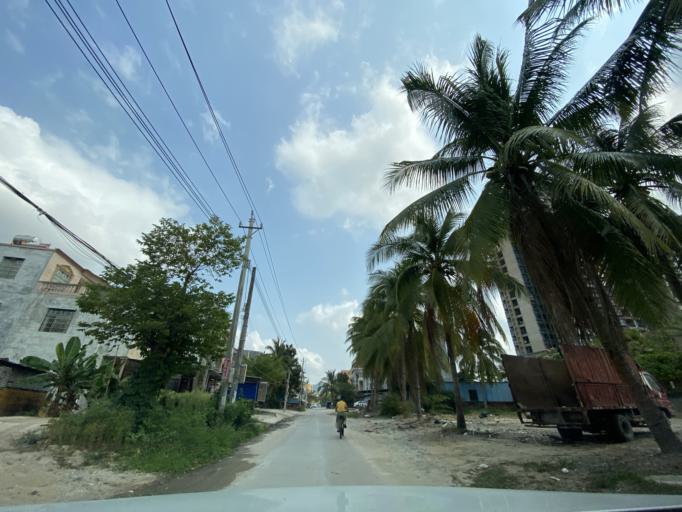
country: CN
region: Hainan
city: Yingzhou
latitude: 18.4180
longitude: 109.8491
